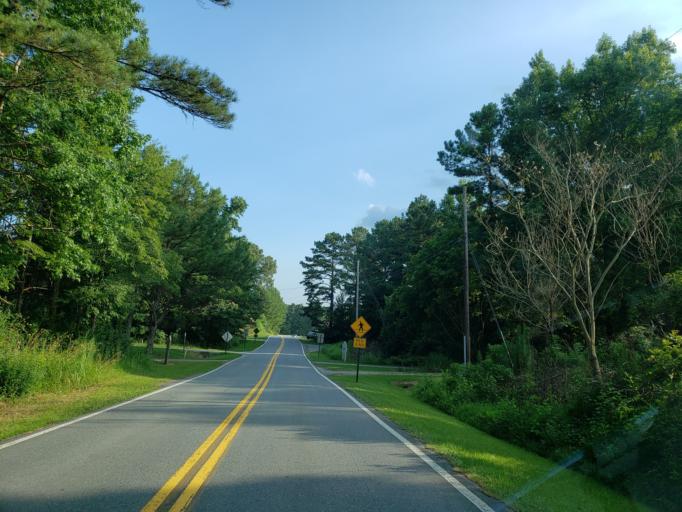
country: US
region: Georgia
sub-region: Polk County
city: Rockmart
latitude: 33.9775
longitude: -85.0043
